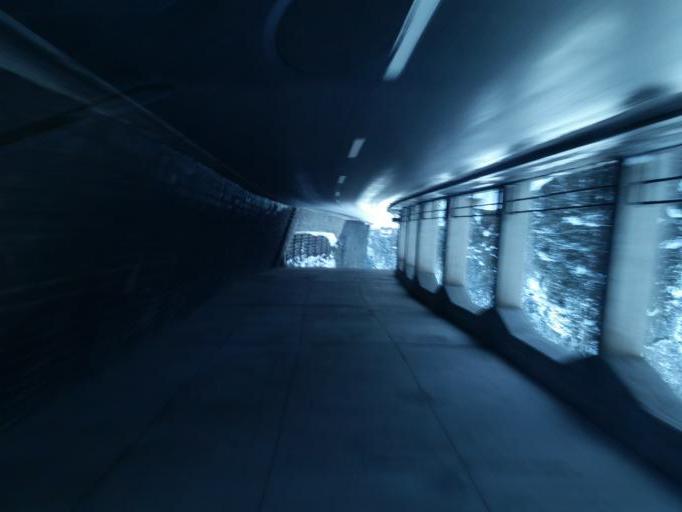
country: CH
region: Grisons
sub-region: Inn District
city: Scuol
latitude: 46.7768
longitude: 10.2335
